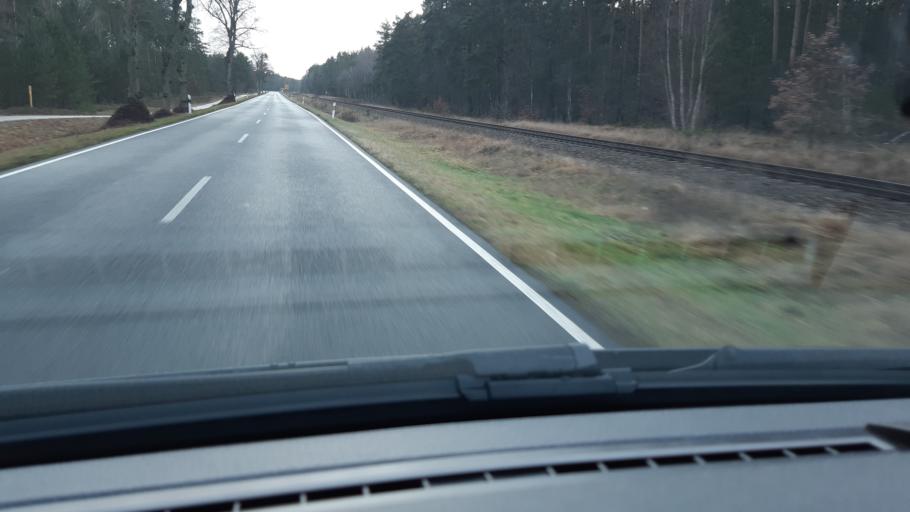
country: DE
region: Brandenburg
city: Zehdenick
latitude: 53.0227
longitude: 13.3758
